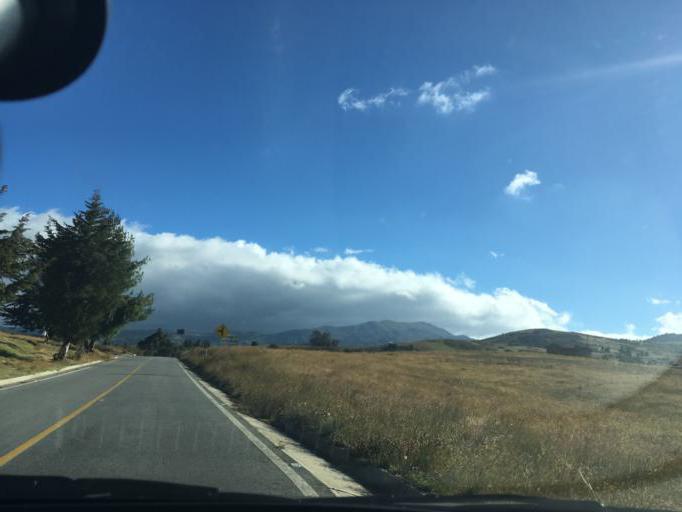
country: CO
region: Boyaca
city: Pesca
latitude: 5.5259
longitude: -72.9774
